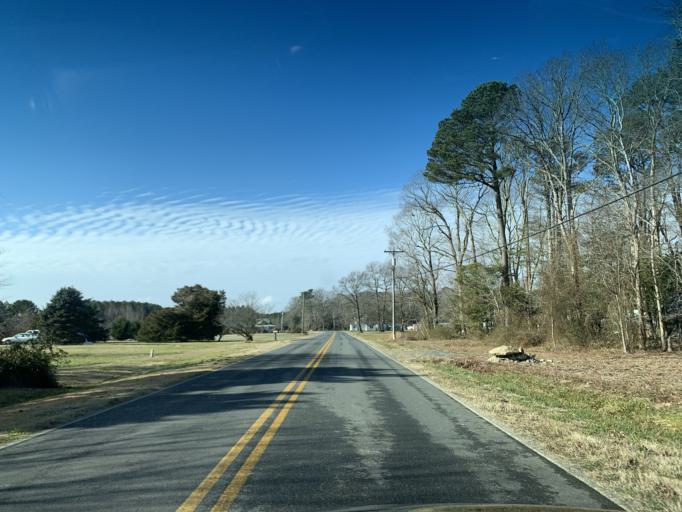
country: US
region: Maryland
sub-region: Worcester County
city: Ocean Pines
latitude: 38.4172
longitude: -75.1332
